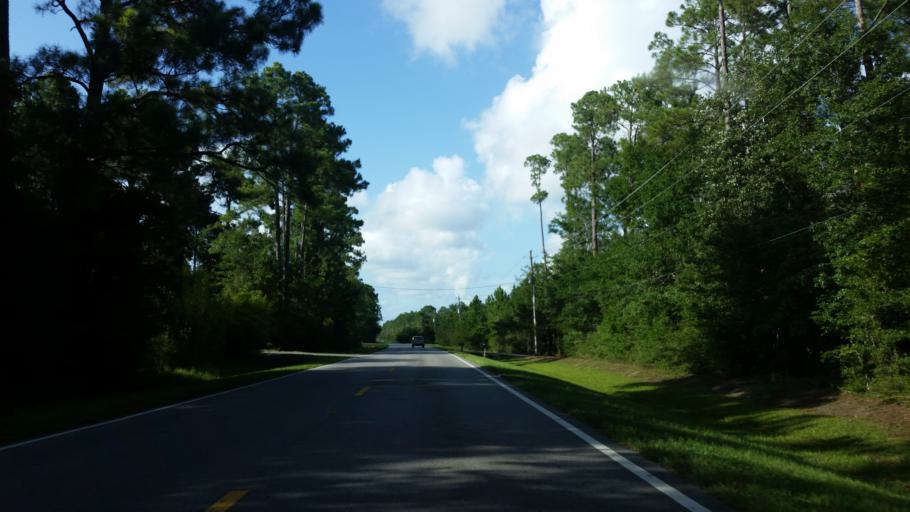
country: US
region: Florida
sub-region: Santa Rosa County
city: Bagdad
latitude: 30.5109
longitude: -87.0563
